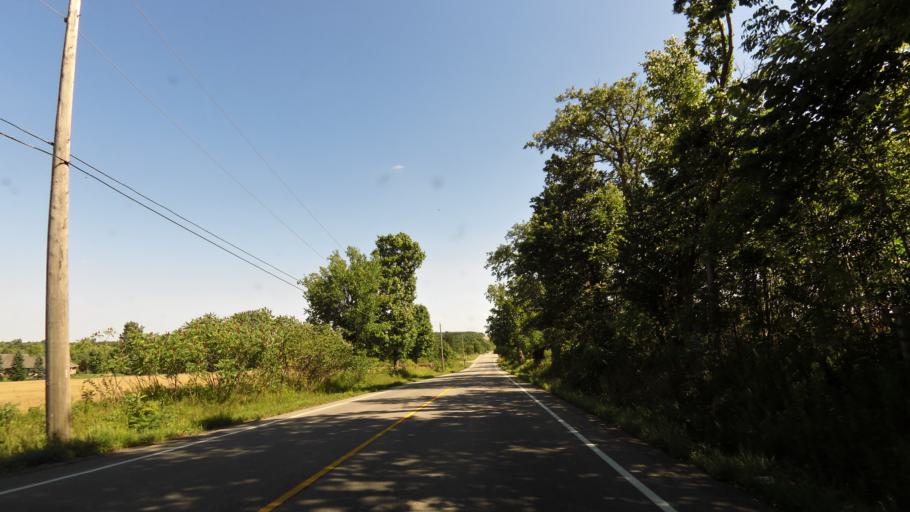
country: CA
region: Ontario
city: Brampton
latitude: 43.7436
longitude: -79.9336
